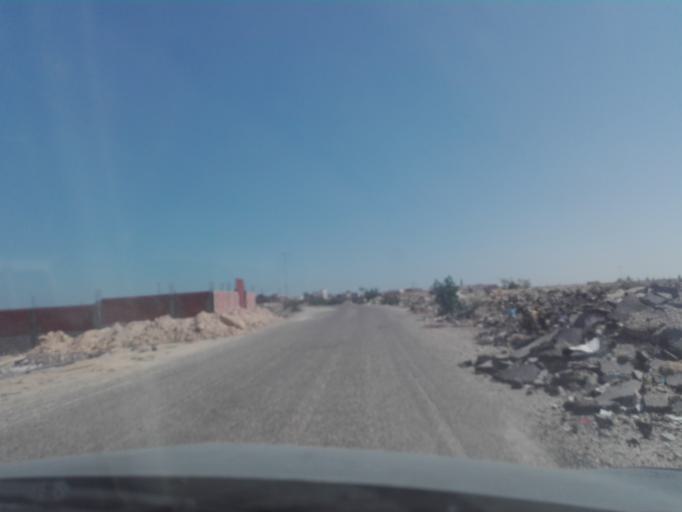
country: TN
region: Qabis
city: Gabes
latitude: 33.8708
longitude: 10.0423
